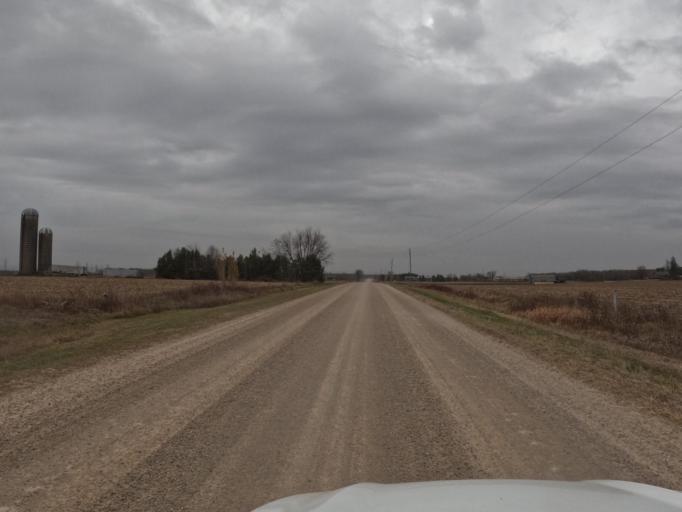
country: CA
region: Ontario
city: Shelburne
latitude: 43.8838
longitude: -80.3586
